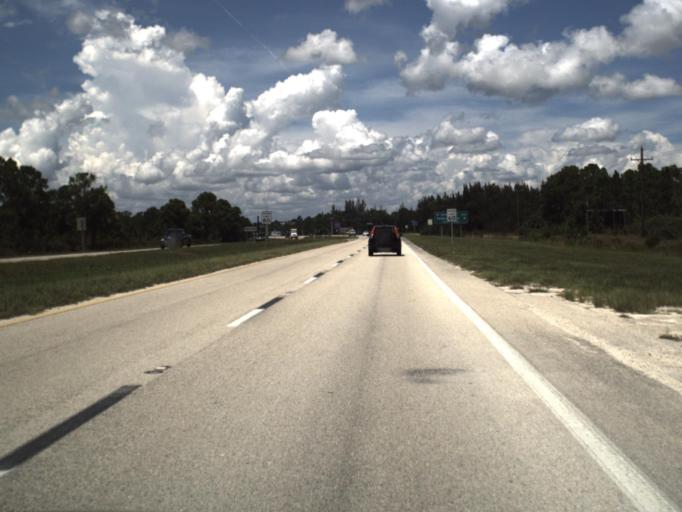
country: US
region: Florida
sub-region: Charlotte County
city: Charlotte Park
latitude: 26.8549
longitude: -81.9856
